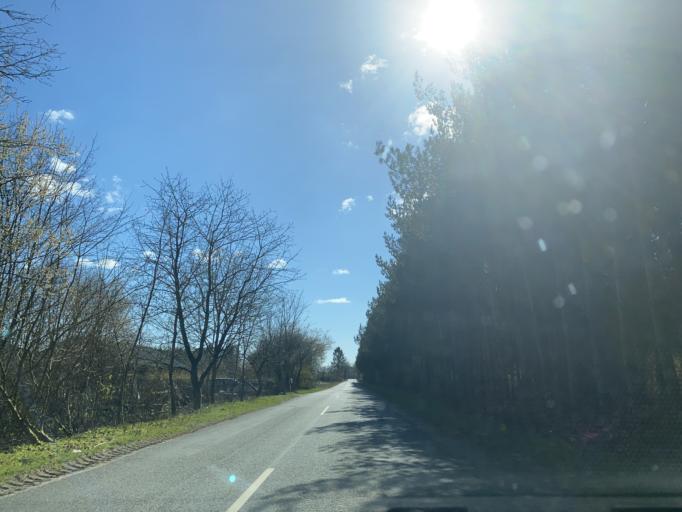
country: DK
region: Central Jutland
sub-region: Silkeborg Kommune
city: Svejbaek
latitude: 56.2419
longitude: 9.6612
